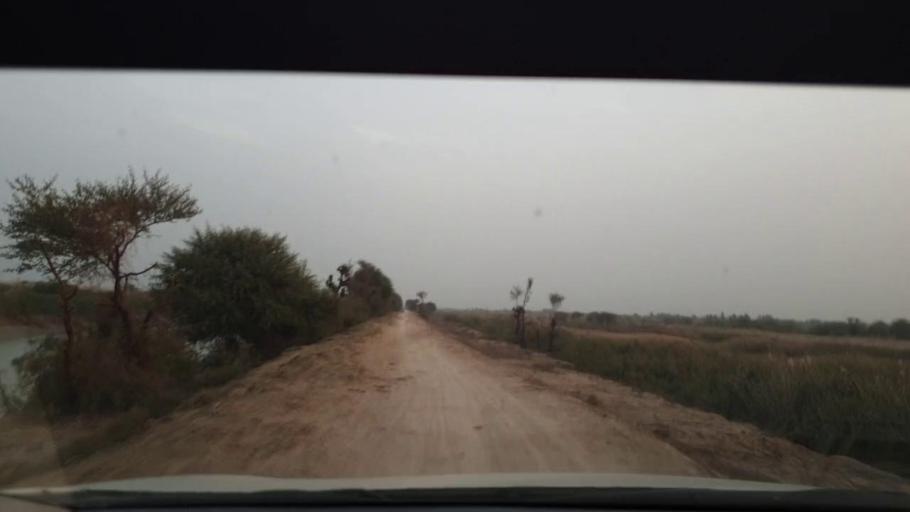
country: PK
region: Sindh
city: Berani
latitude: 25.8614
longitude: 68.7755
